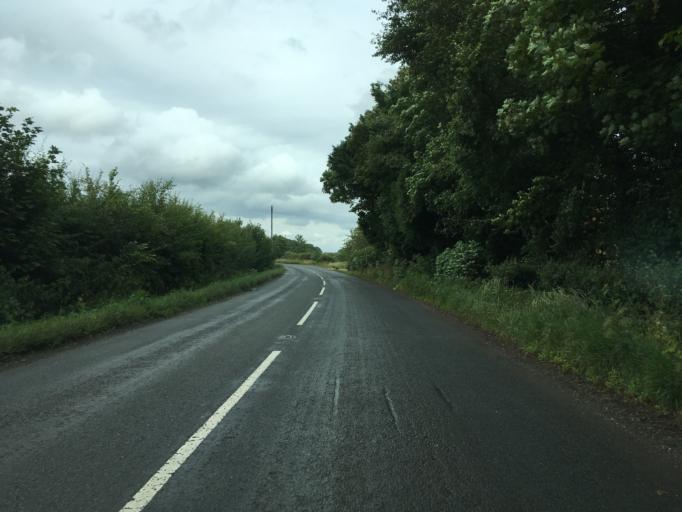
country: GB
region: England
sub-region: Gloucestershire
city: Winchcombe
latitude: 52.0045
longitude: -1.9583
